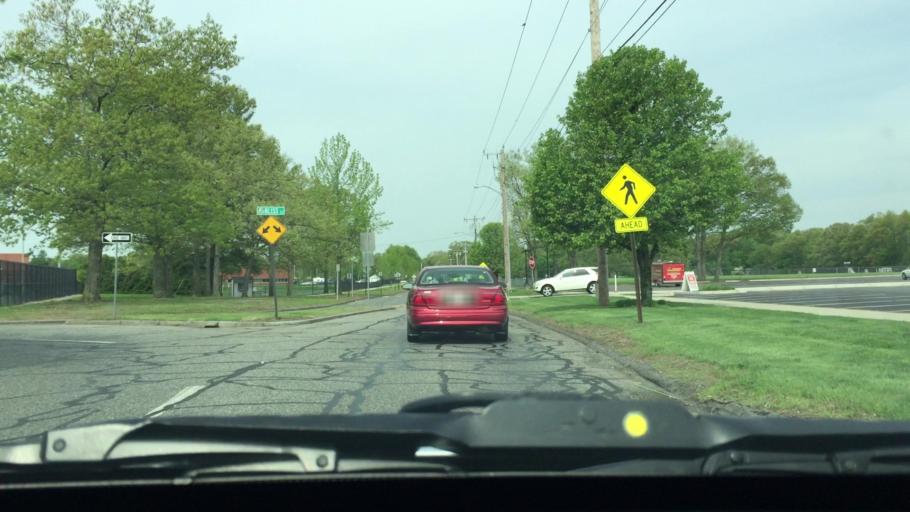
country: US
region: Massachusetts
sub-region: Hampden County
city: Longmeadow
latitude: 42.0566
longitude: -72.5559
